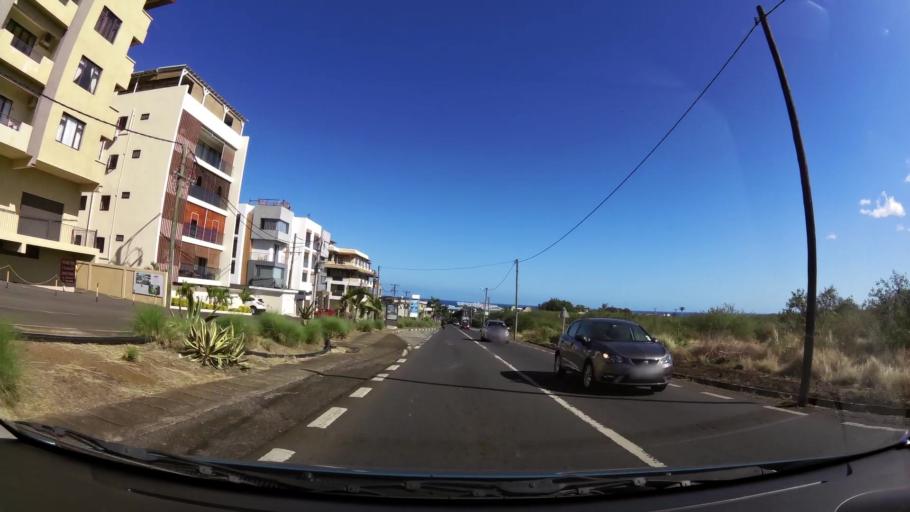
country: MU
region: Black River
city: Flic en Flac
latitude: -20.2764
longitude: 57.3788
